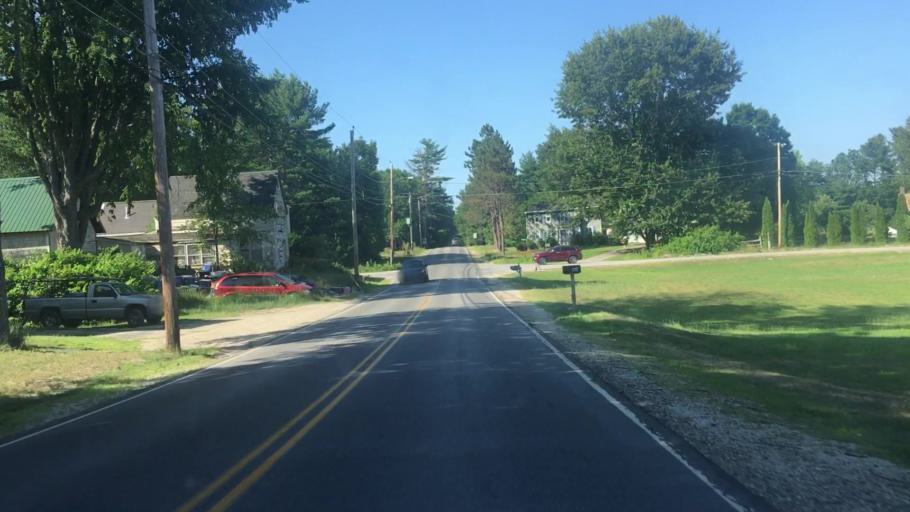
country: US
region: Maine
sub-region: York County
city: Buxton
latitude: 43.7131
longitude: -70.5705
